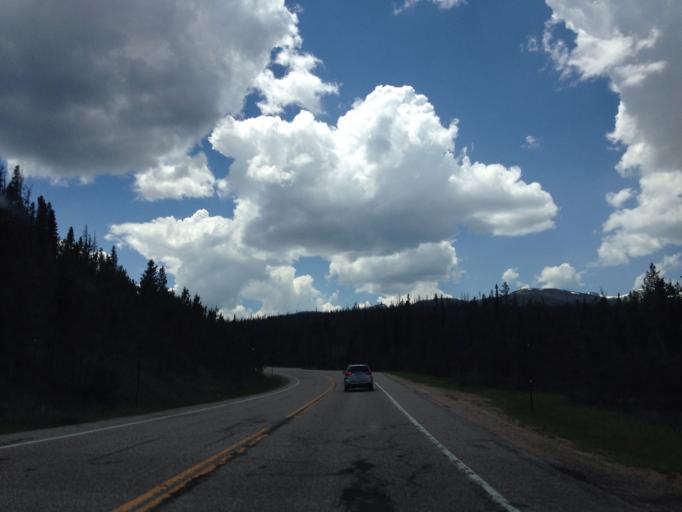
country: US
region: Colorado
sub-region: Larimer County
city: Estes Park
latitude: 40.6005
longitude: -105.8370
